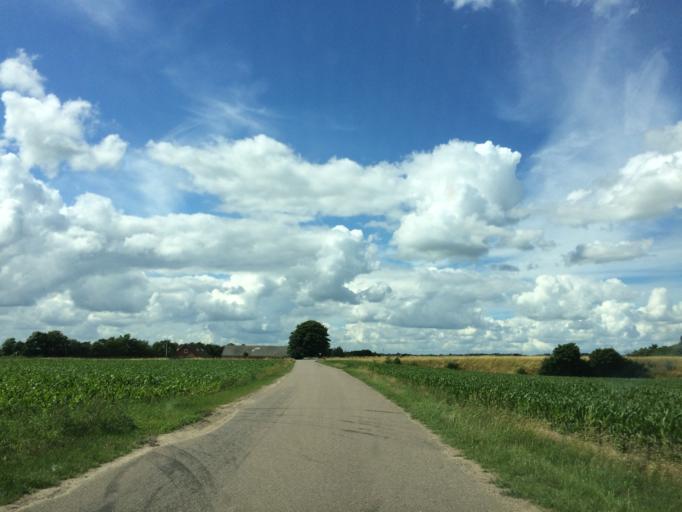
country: DK
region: North Denmark
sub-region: Vesthimmerland Kommune
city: Alestrup
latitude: 56.5679
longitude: 9.4893
